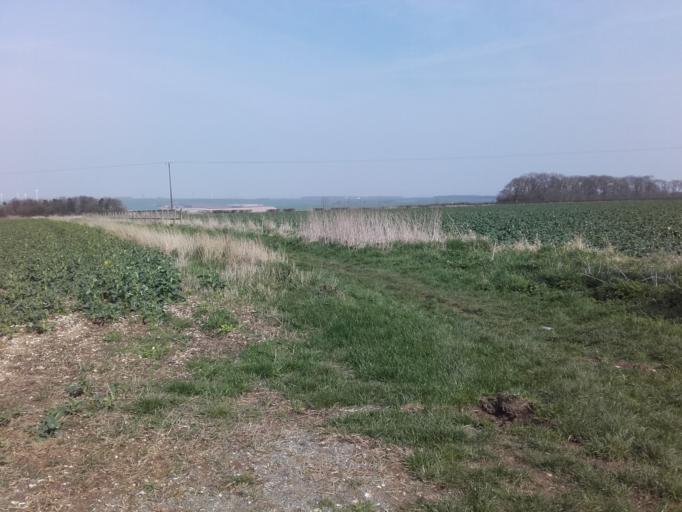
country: GB
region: England
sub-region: East Riding of Yorkshire
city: South Cave
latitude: 53.8032
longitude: -0.5733
